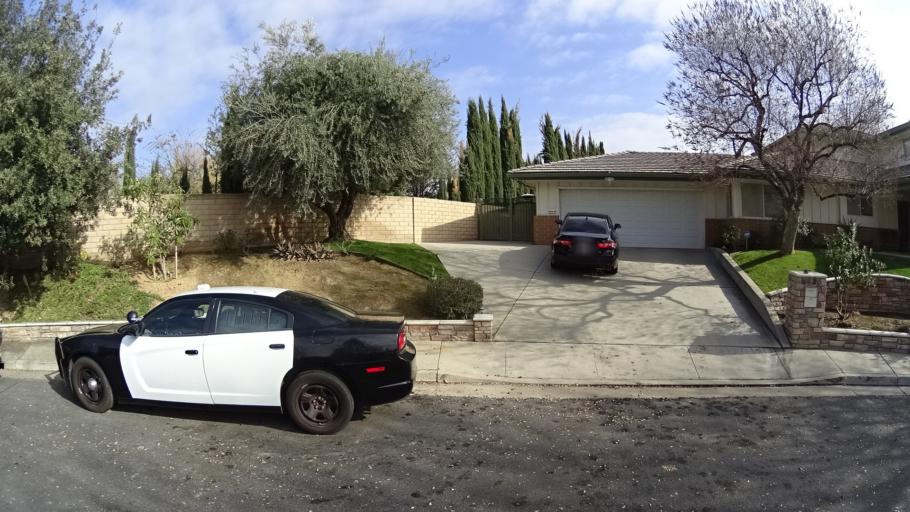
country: US
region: California
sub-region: Kern County
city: Bakersfield
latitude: 35.3956
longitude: -118.9314
